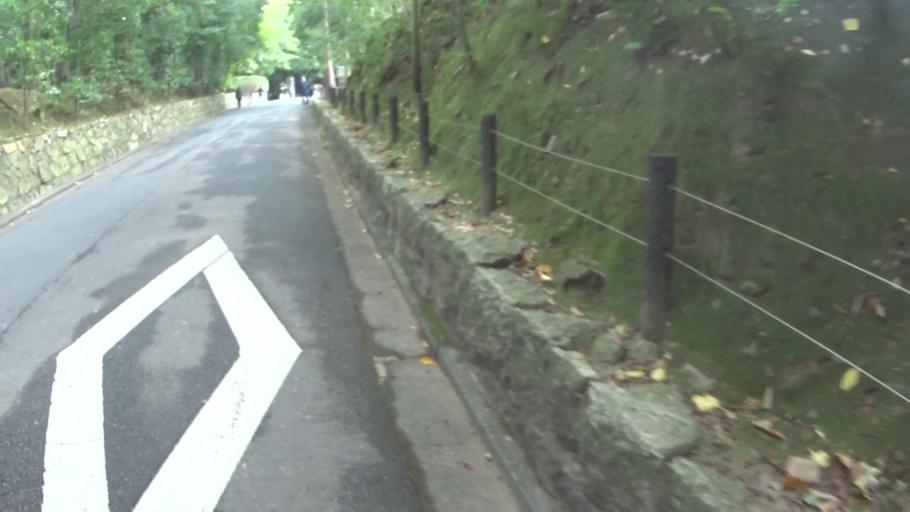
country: JP
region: Kyoto
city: Kyoto
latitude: 34.9800
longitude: 135.7787
